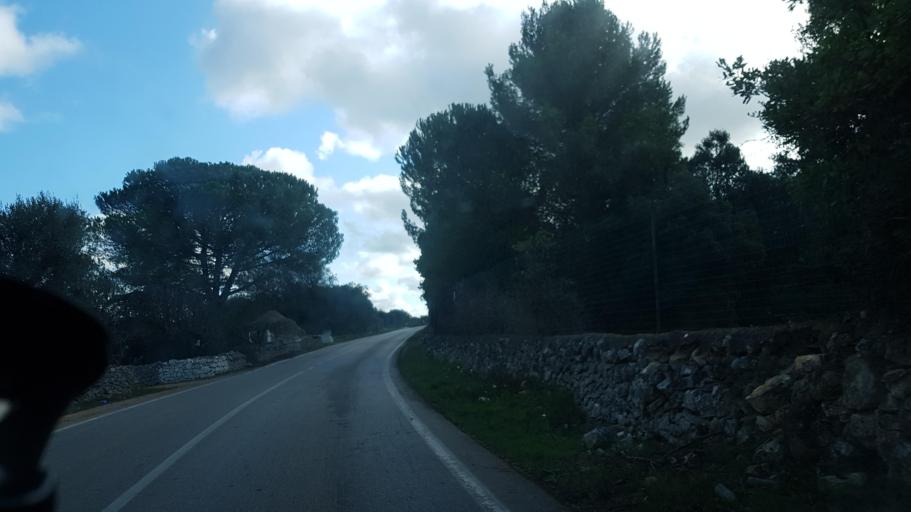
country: IT
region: Apulia
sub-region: Provincia di Brindisi
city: Ostuni
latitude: 40.6782
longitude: 17.5917
